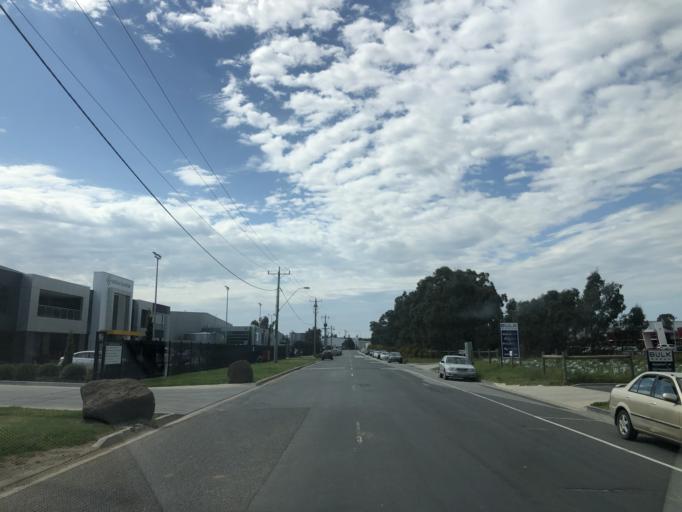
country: AU
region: Victoria
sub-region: Casey
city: Hampton Park
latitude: -38.0368
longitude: 145.2284
